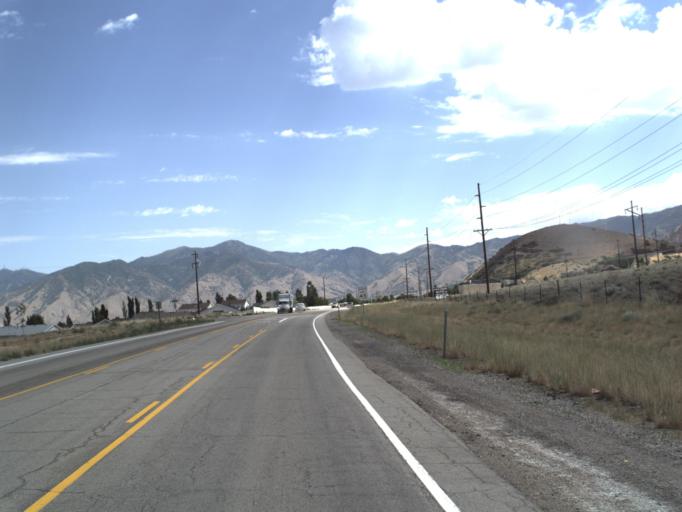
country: US
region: Utah
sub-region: Tooele County
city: Tooele
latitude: 40.5113
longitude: -112.3128
